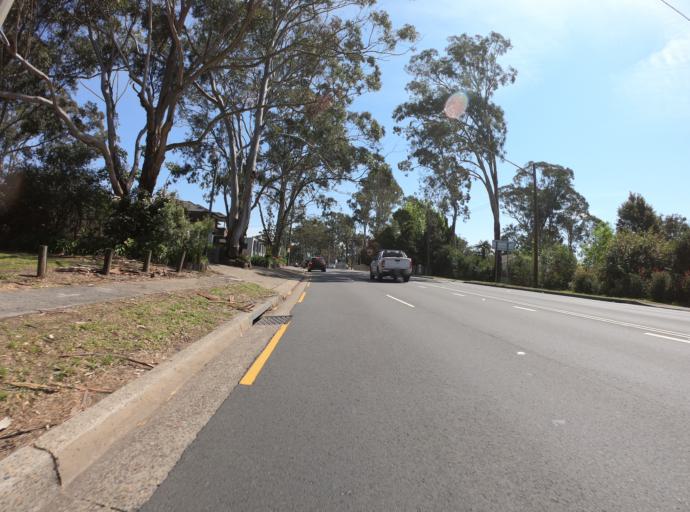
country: AU
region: New South Wales
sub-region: The Hills Shire
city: West Pennant
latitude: -33.7444
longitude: 151.0479
